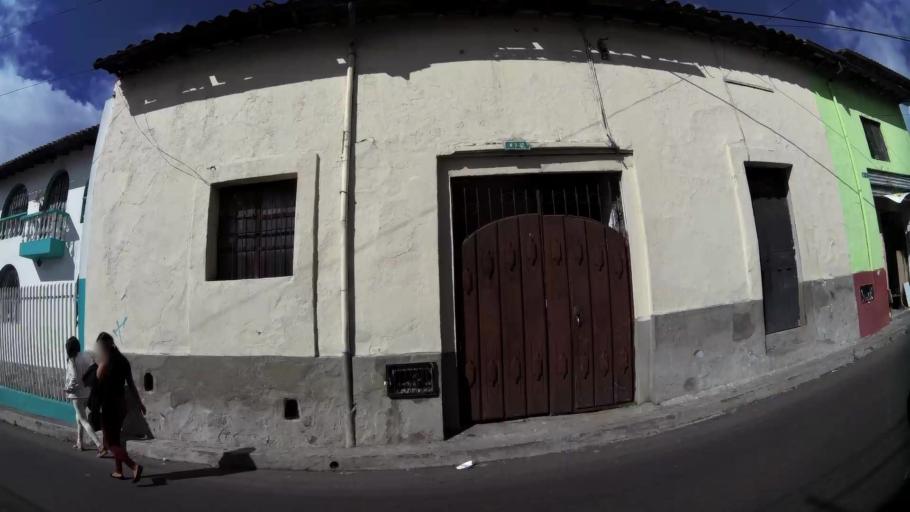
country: EC
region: Pichincha
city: Quito
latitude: -0.2263
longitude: -78.5046
